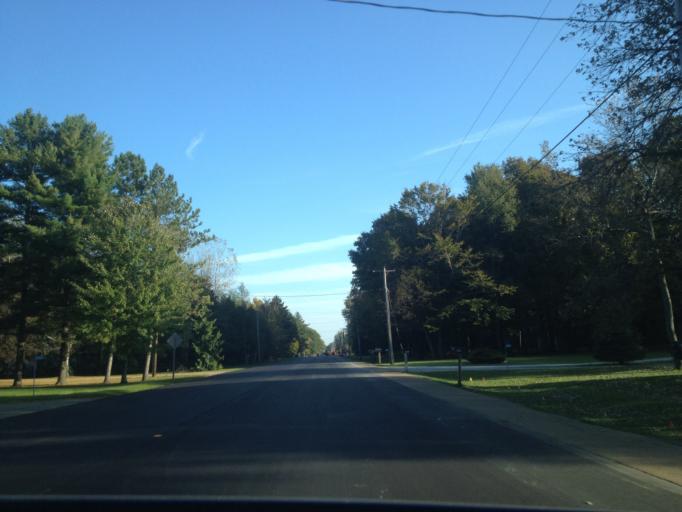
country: CA
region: Ontario
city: Delaware
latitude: 42.5777
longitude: -81.5747
